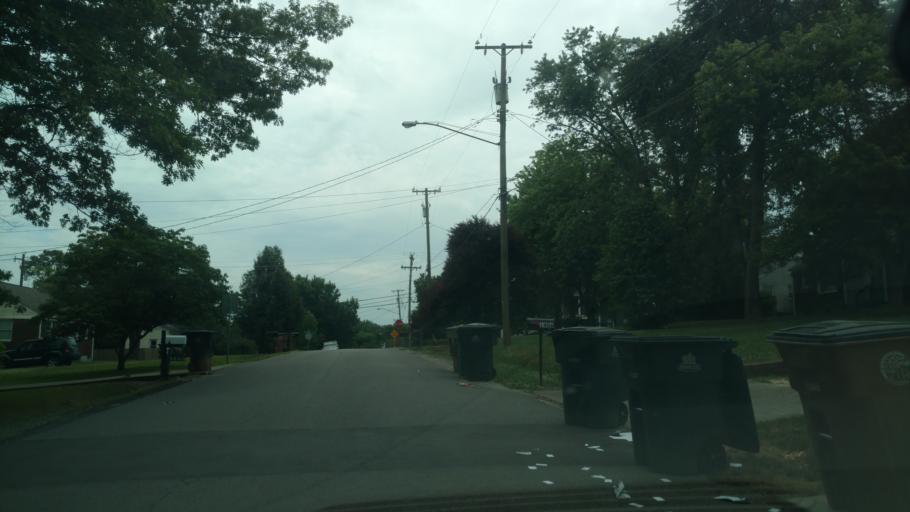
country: US
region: Tennessee
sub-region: Davidson County
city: Nashville
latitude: 36.1920
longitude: -86.7189
